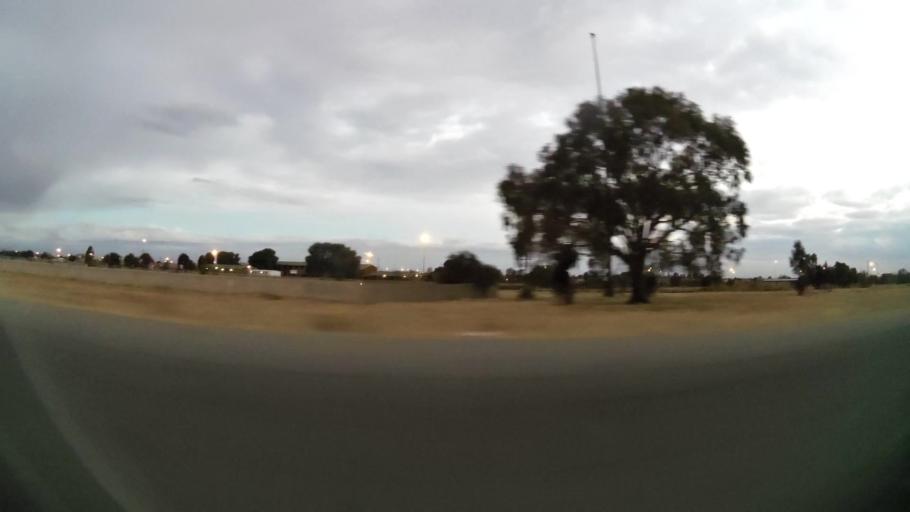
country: ZA
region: Orange Free State
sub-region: Lejweleputswa District Municipality
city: Welkom
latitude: -27.9530
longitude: 26.7895
